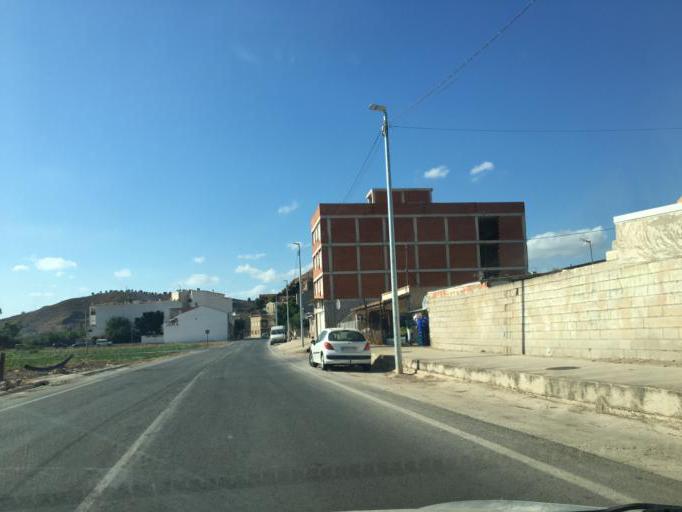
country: ES
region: Murcia
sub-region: Murcia
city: Murcia
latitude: 38.0212
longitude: -1.0869
